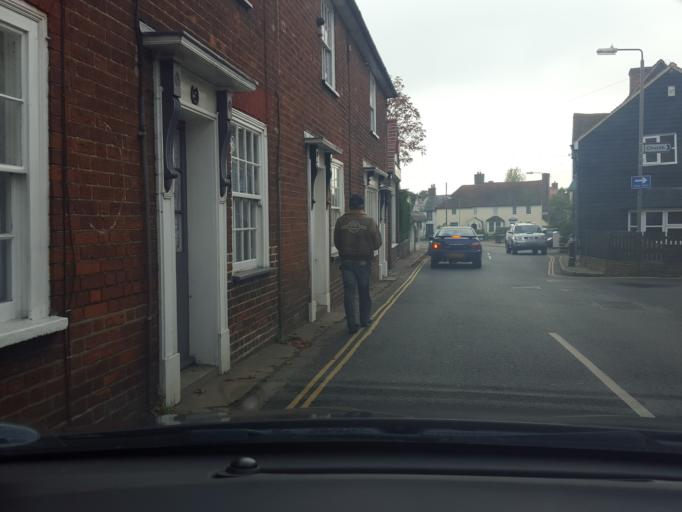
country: GB
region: England
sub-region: Essex
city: Saint Osyth
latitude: 51.7990
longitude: 1.0778
